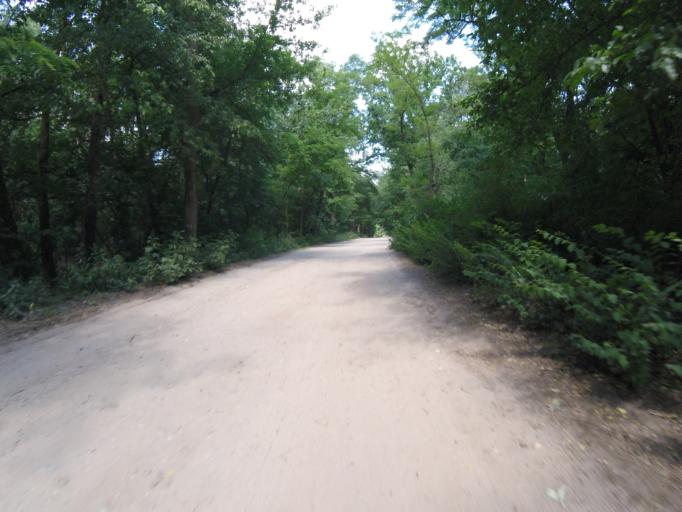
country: DE
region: Brandenburg
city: Bestensee
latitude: 52.2694
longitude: 13.6575
